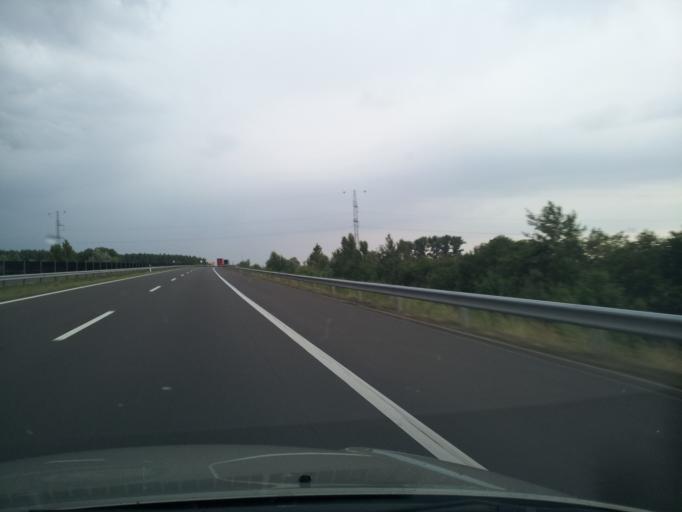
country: HU
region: Heves
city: Fuzesabony
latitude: 47.7442
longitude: 20.4452
